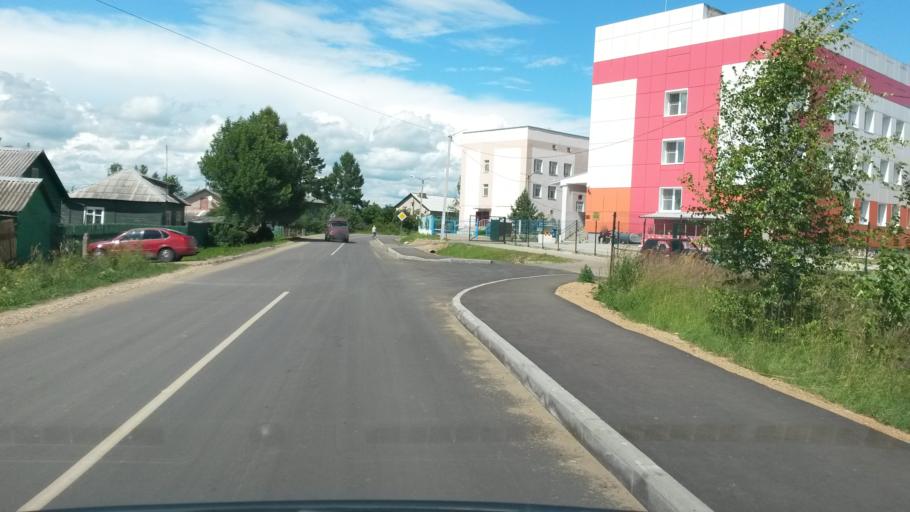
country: RU
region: Jaroslavl
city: Gavrilov-Yam
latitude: 57.3103
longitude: 39.8658
